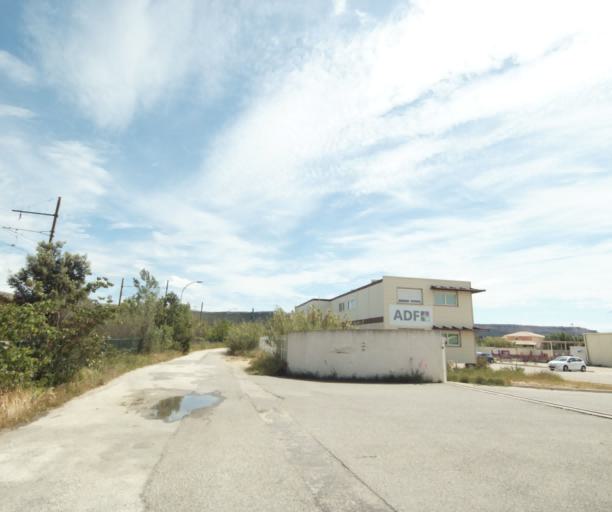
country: FR
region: Provence-Alpes-Cote d'Azur
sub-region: Departement des Bouches-du-Rhone
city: Rognac
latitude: 43.5023
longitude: 5.2211
